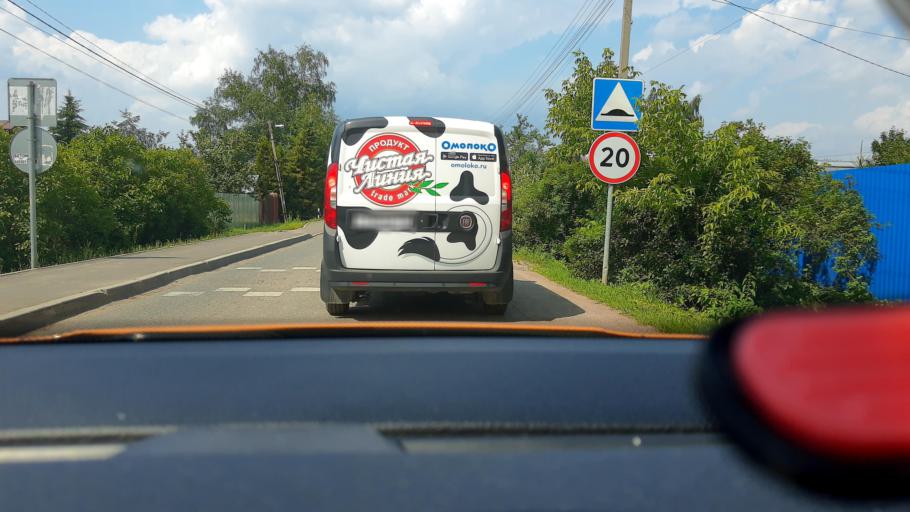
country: RU
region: Moskovskaya
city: Povedniki
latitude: 56.0022
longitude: 37.5897
